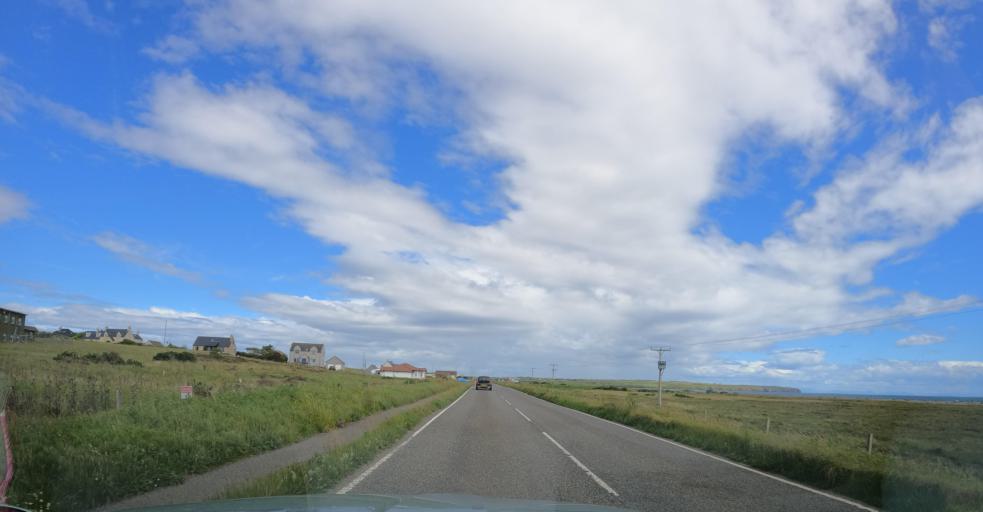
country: GB
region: Scotland
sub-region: Eilean Siar
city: Stornoway
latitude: 58.2038
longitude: -6.3213
